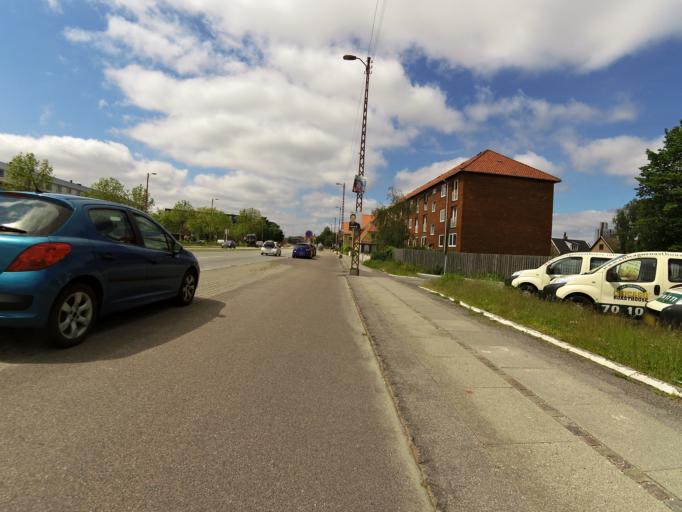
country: DK
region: Capital Region
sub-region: Herlev Kommune
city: Herlev
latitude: 55.7208
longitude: 12.4479
